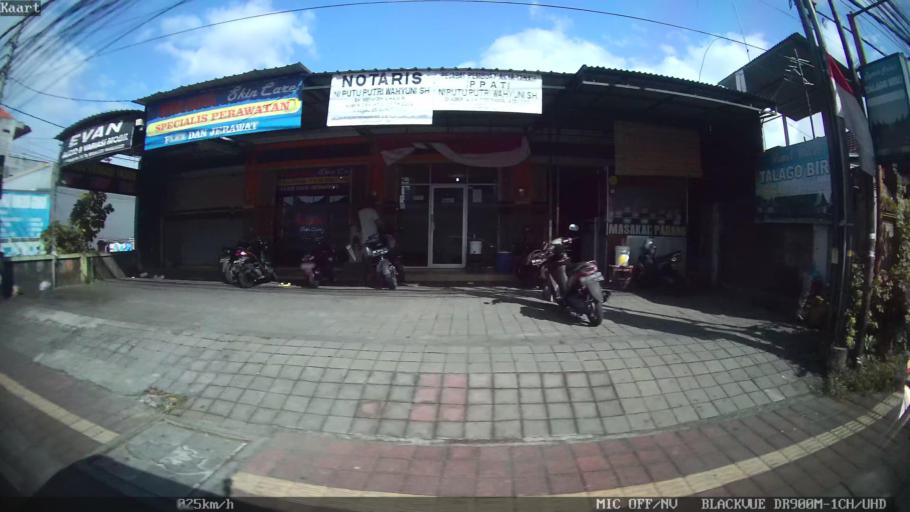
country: ID
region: Bali
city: Karyadharma
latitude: -8.6851
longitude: 115.2066
